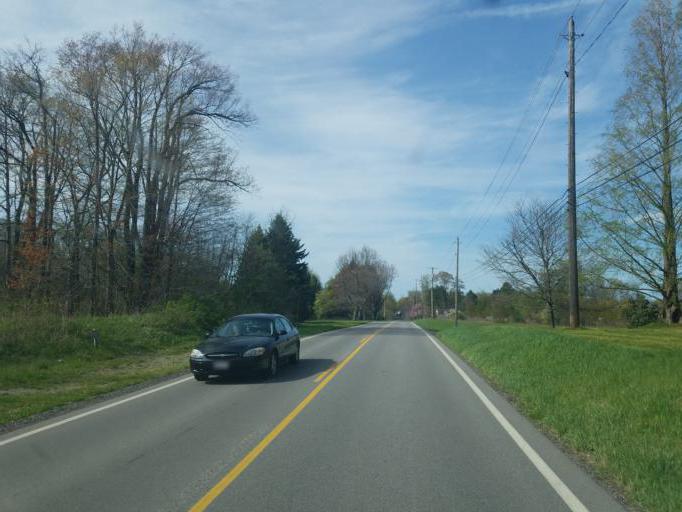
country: US
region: Ohio
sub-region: Lake County
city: North Madison
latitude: 41.8129
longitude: -81.0947
